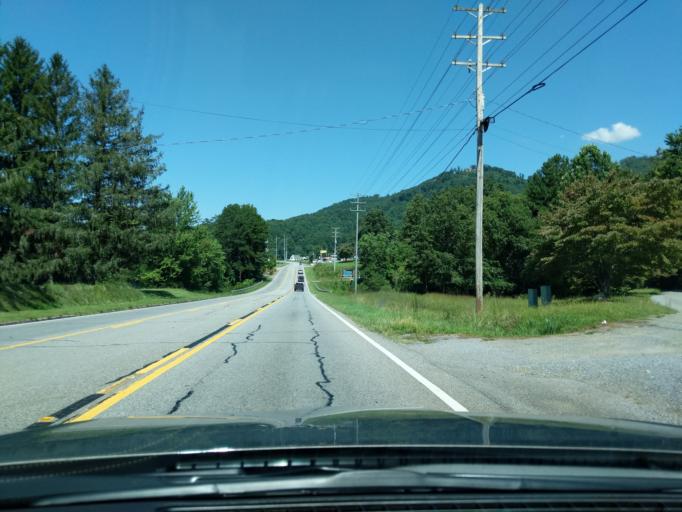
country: US
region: Georgia
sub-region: Towns County
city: Hiawassee
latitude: 34.9345
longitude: -83.7367
